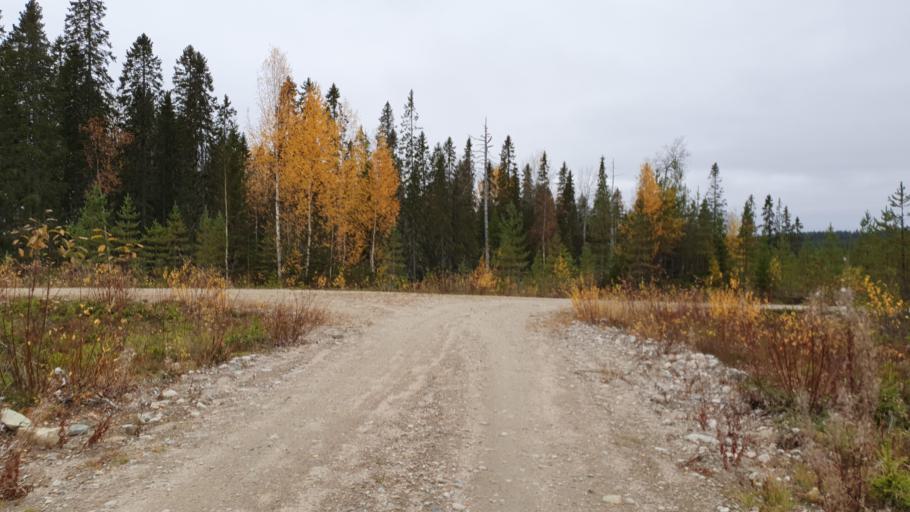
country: FI
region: Kainuu
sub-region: Kehys-Kainuu
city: Kuhmo
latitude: 64.4502
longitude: 29.6091
